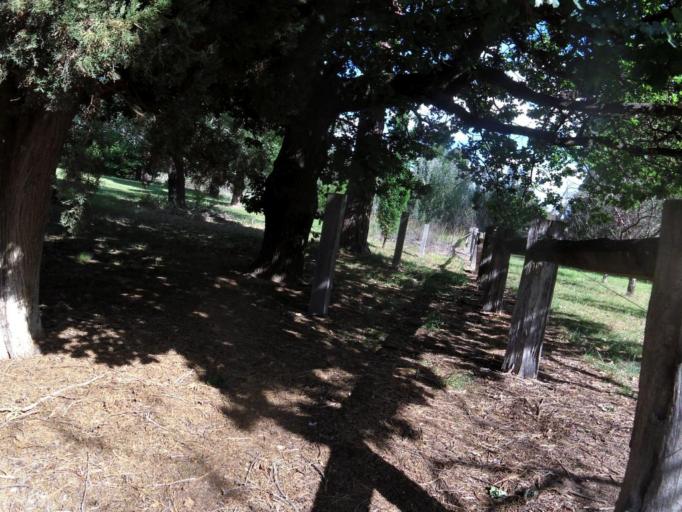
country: AU
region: Australian Capital Territory
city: Belconnen
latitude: -35.1721
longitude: 149.0714
